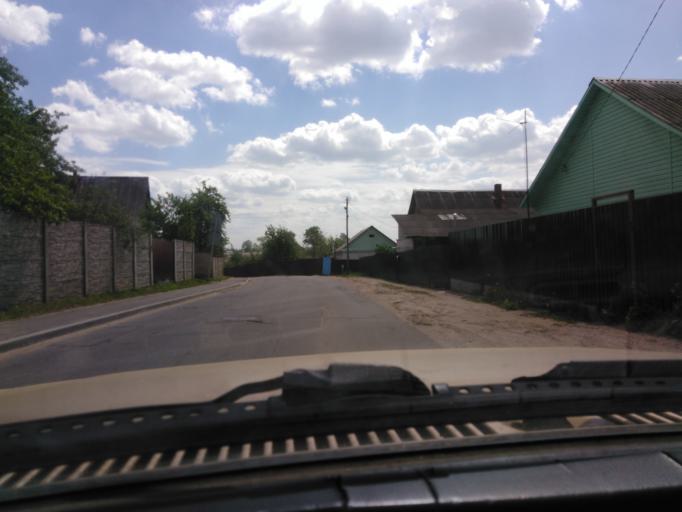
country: BY
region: Mogilev
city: Mahilyow
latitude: 53.9343
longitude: 30.3250
